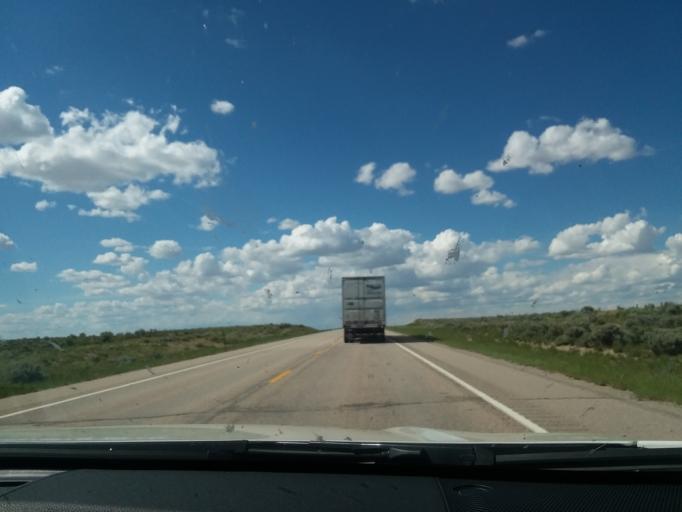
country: US
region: Wyoming
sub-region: Sweetwater County
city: North Rock Springs
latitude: 41.8799
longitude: -109.3498
